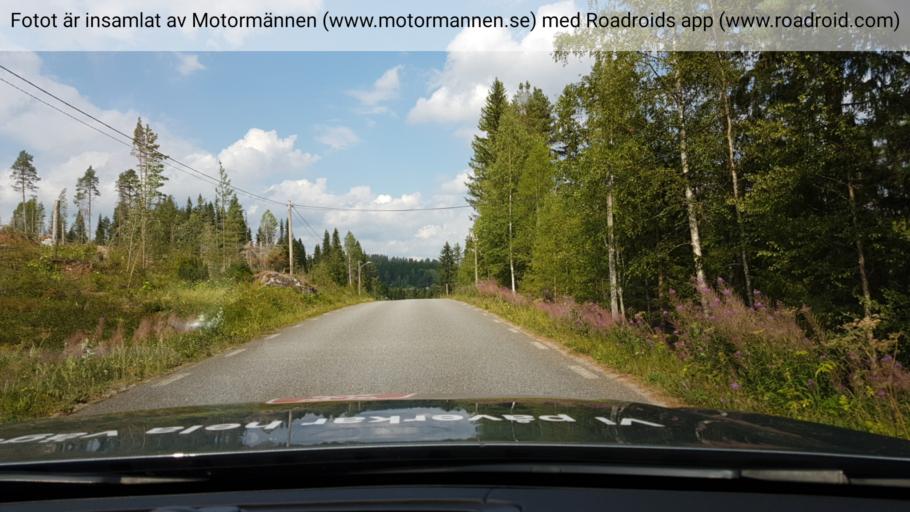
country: SE
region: Jaemtland
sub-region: OEstersunds Kommun
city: Brunflo
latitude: 62.9761
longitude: 15.1302
